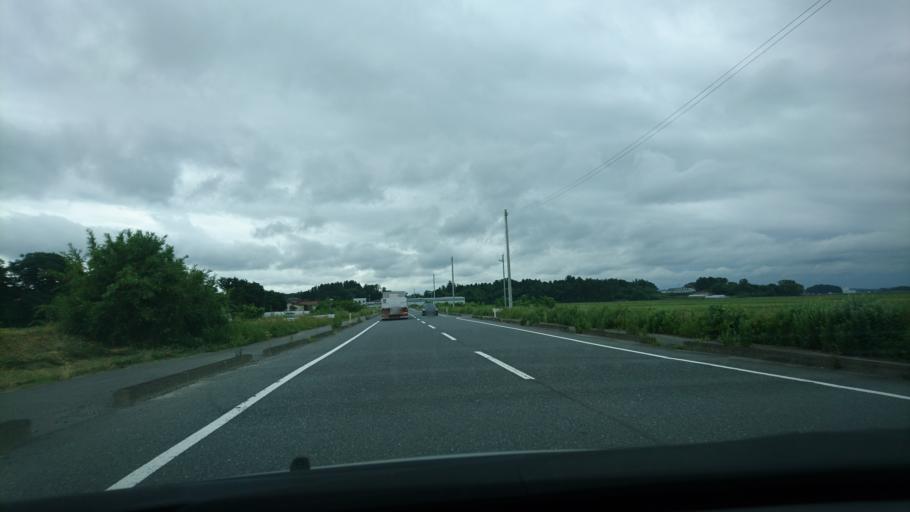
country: JP
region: Iwate
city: Ichinoseki
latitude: 38.7457
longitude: 141.2561
